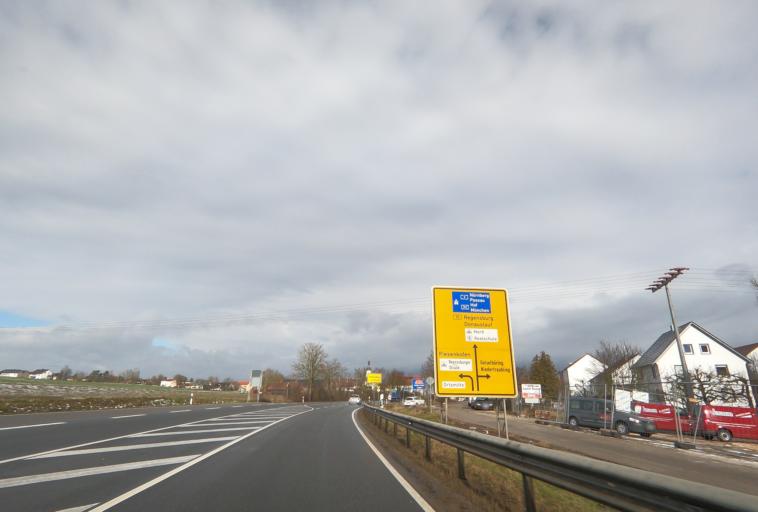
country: DE
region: Bavaria
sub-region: Upper Palatinate
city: Obertraubling
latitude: 48.9616
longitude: 12.1694
